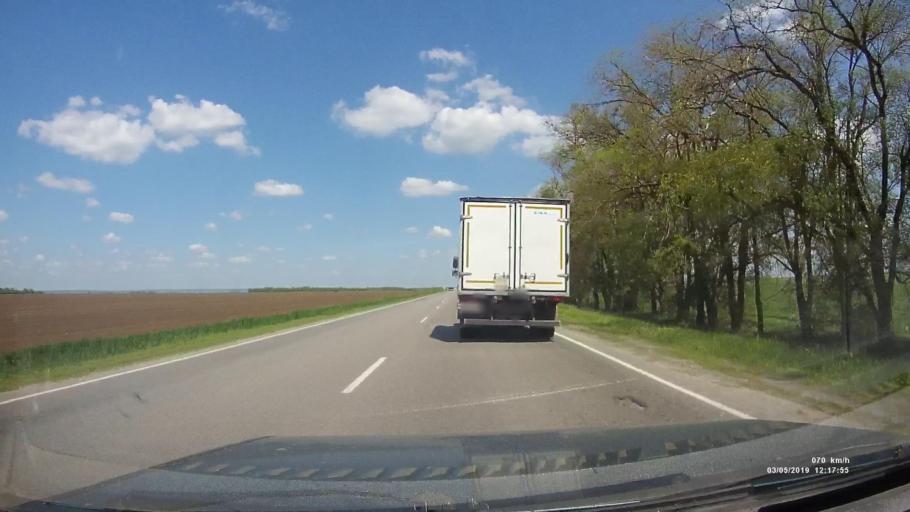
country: RU
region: Rostov
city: Melikhovskaya
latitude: 47.3873
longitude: 40.5957
